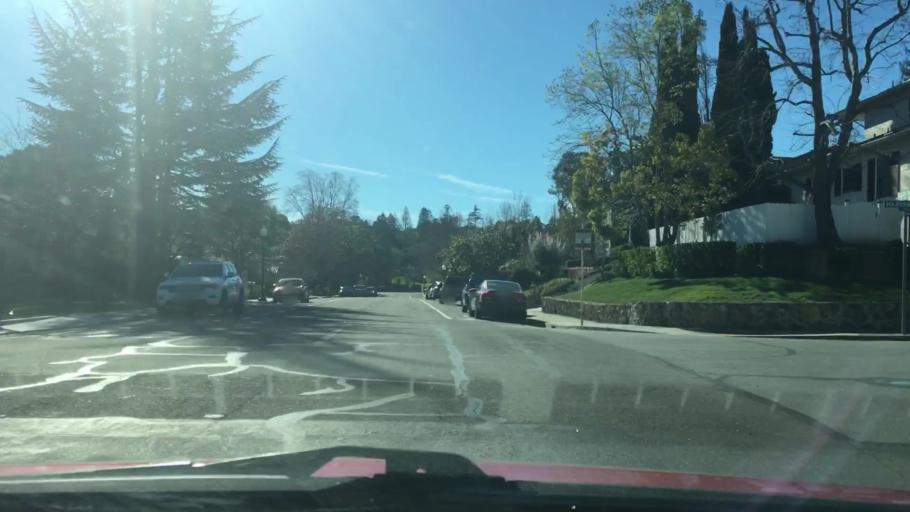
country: US
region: California
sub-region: San Mateo County
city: San Mateo
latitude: 37.5530
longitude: -122.3265
